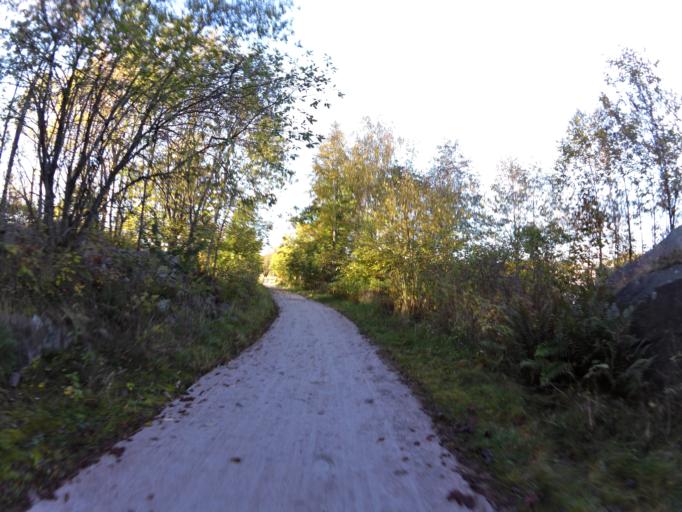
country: NO
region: Ostfold
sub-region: Sarpsborg
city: Sarpsborg
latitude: 59.2651
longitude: 11.1028
